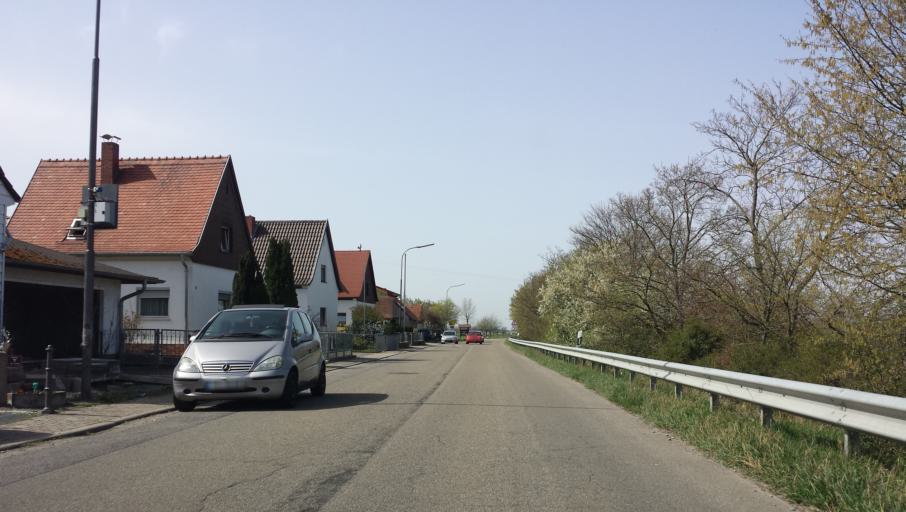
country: DE
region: Rheinland-Pfalz
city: Otterstadt
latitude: 49.3767
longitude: 8.4461
